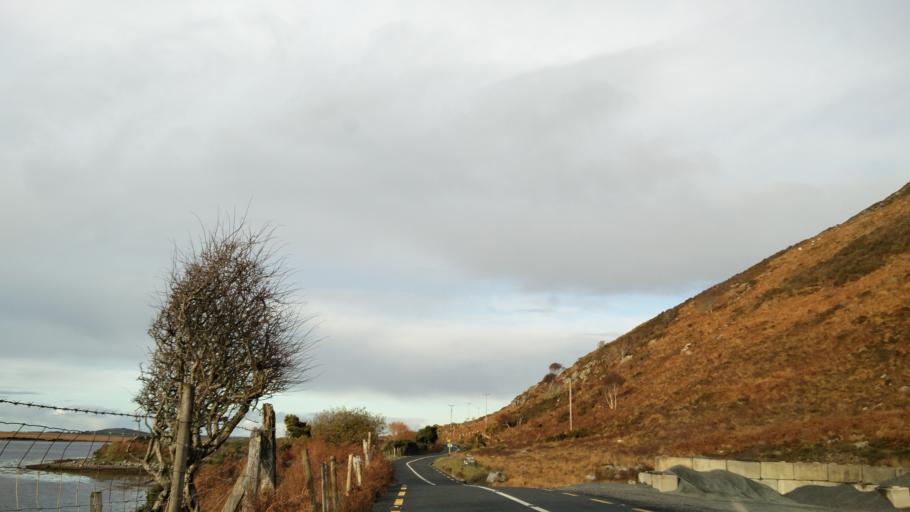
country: IE
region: Connaught
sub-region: Maigh Eo
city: Westport
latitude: 53.9282
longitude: -9.7905
